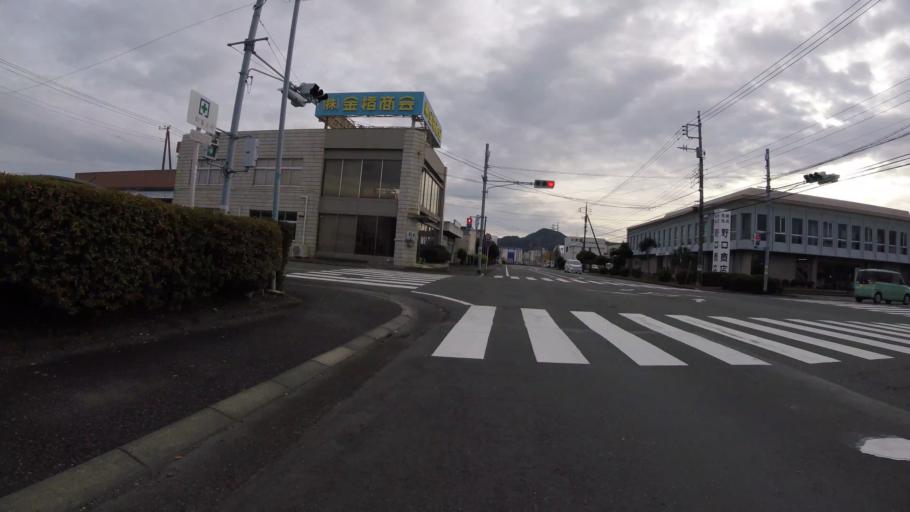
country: JP
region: Shizuoka
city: Mishima
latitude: 35.0953
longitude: 138.9093
